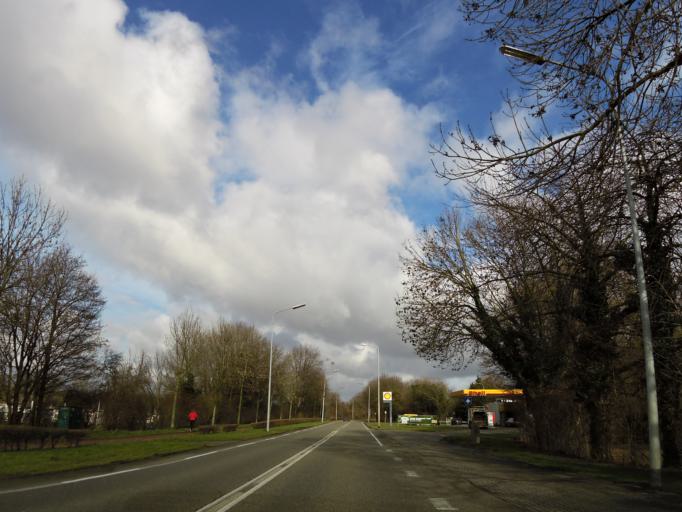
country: NL
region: Limburg
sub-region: Gemeente Maastricht
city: Maastricht
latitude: 50.8287
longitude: 5.7023
